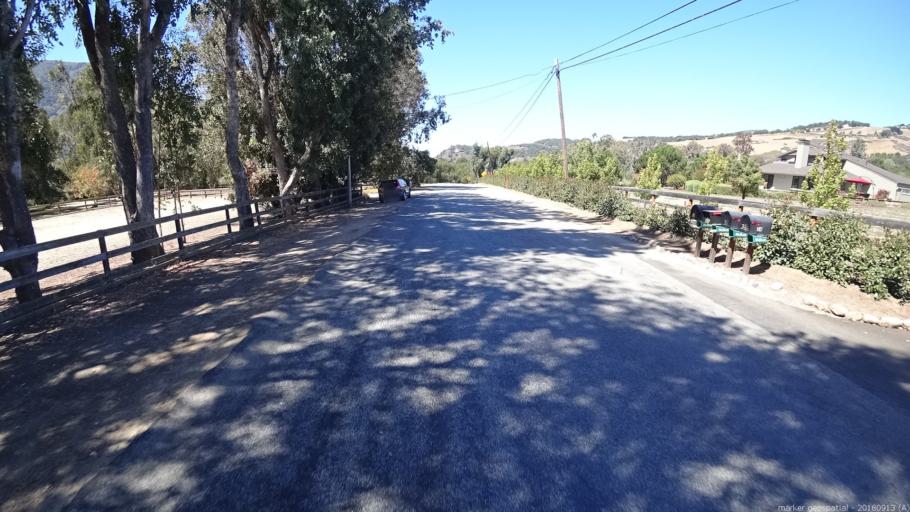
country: US
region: California
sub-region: Monterey County
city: Carmel Valley Village
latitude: 36.5103
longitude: -121.7628
